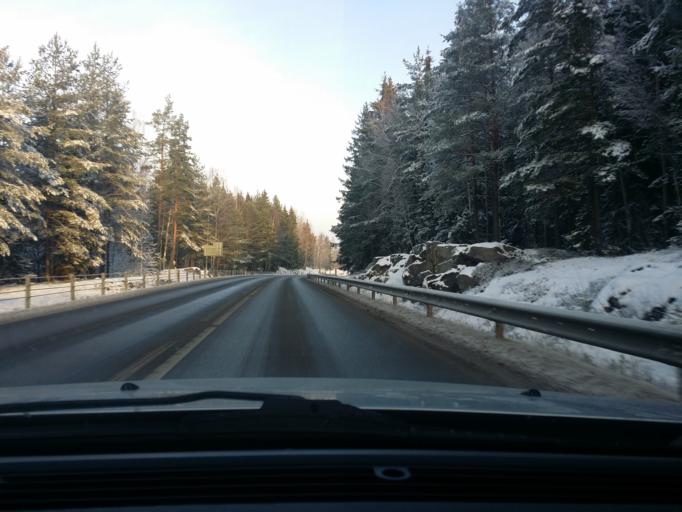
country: SE
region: OErebro
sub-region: Lindesbergs Kommun
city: Frovi
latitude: 59.4933
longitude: 15.3754
